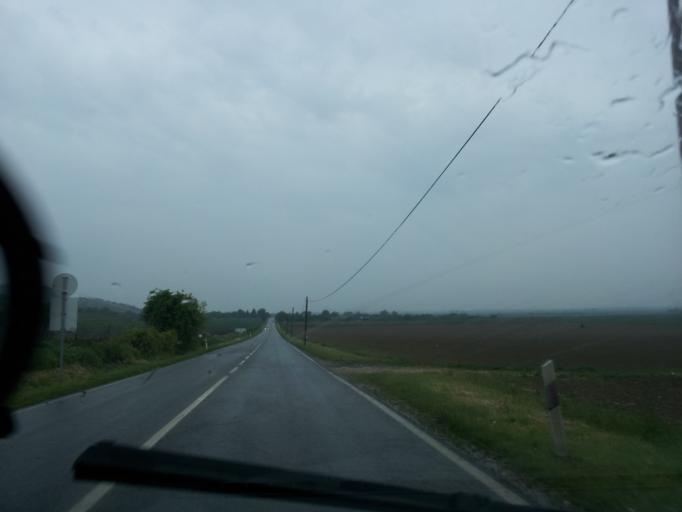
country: HU
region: Tolna
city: Szekszard
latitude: 46.2956
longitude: 18.6864
